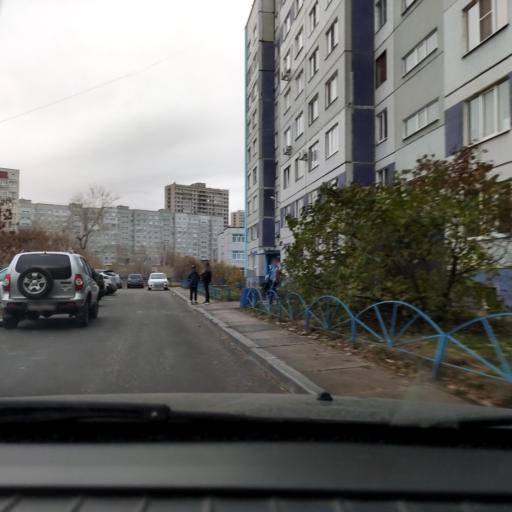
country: RU
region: Samara
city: Zhigulevsk
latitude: 53.4835
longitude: 49.5185
